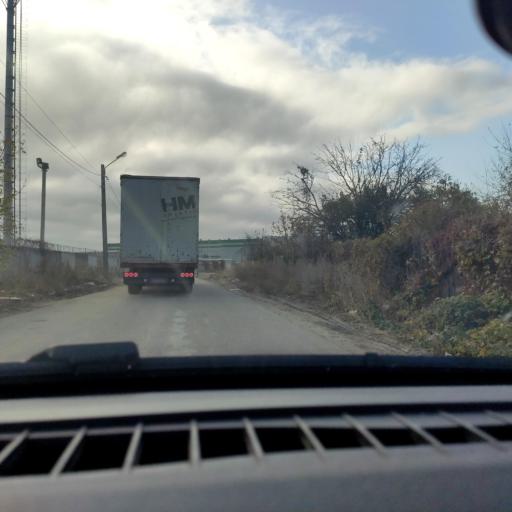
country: RU
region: Voronezj
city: Maslovka
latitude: 51.5975
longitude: 39.2341
